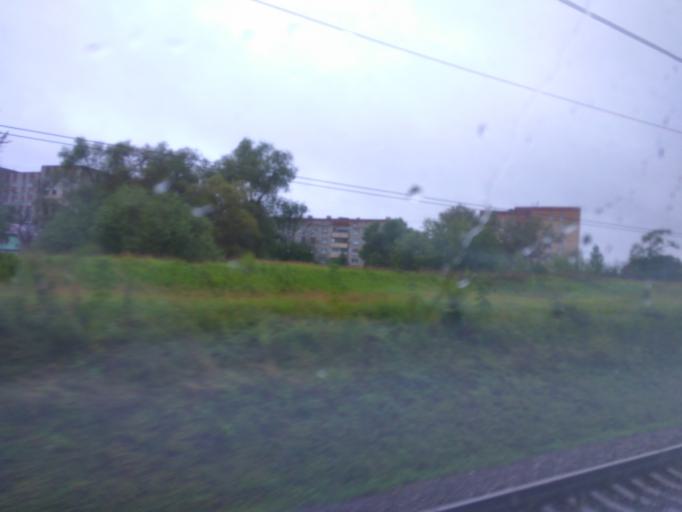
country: RU
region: Moskovskaya
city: Stupino
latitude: 54.9000
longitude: 38.0880
